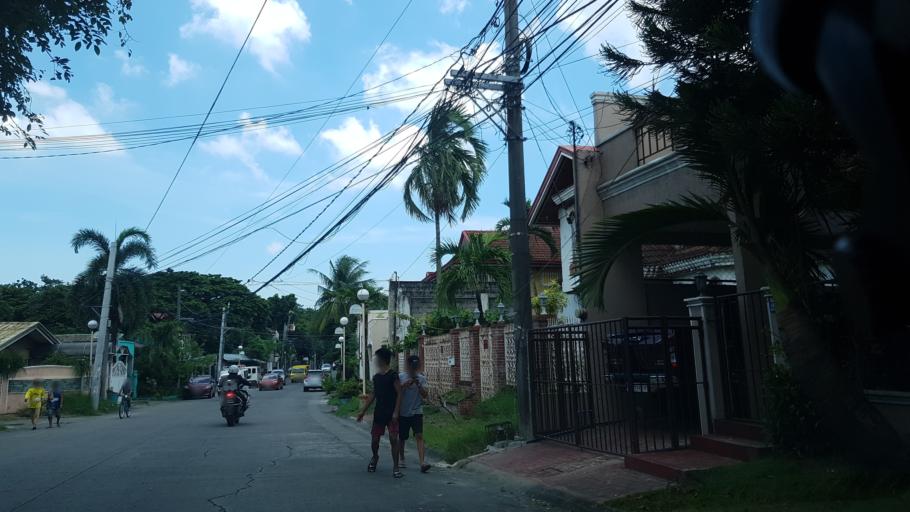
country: PH
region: Calabarzon
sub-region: Province of Rizal
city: Las Pinas
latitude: 14.4318
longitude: 120.9869
